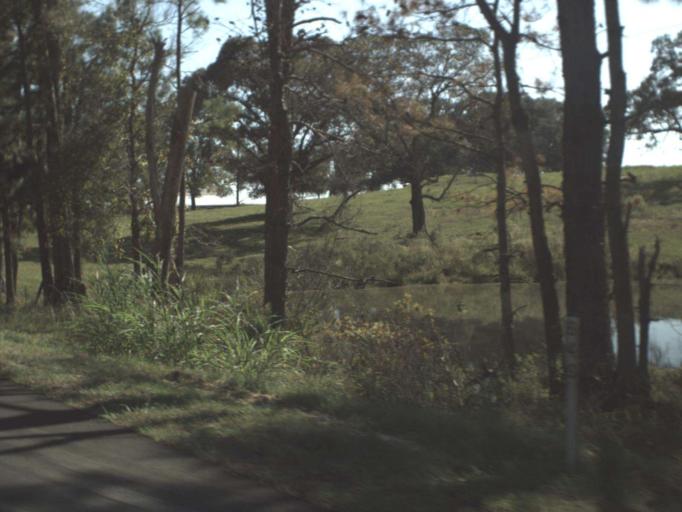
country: US
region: Alabama
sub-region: Covington County
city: Florala
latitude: 30.8528
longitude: -86.2454
